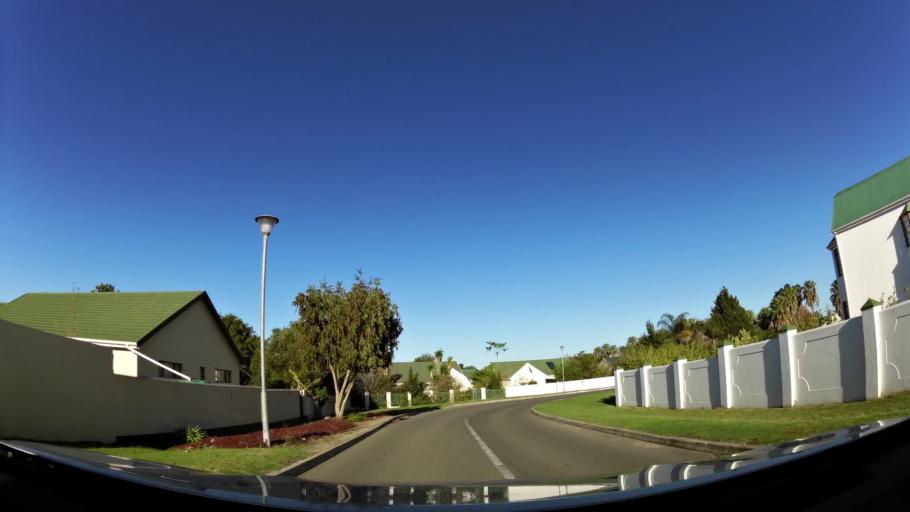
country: ZA
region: Western Cape
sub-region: Eden District Municipality
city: George
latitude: -33.9605
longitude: 22.4439
